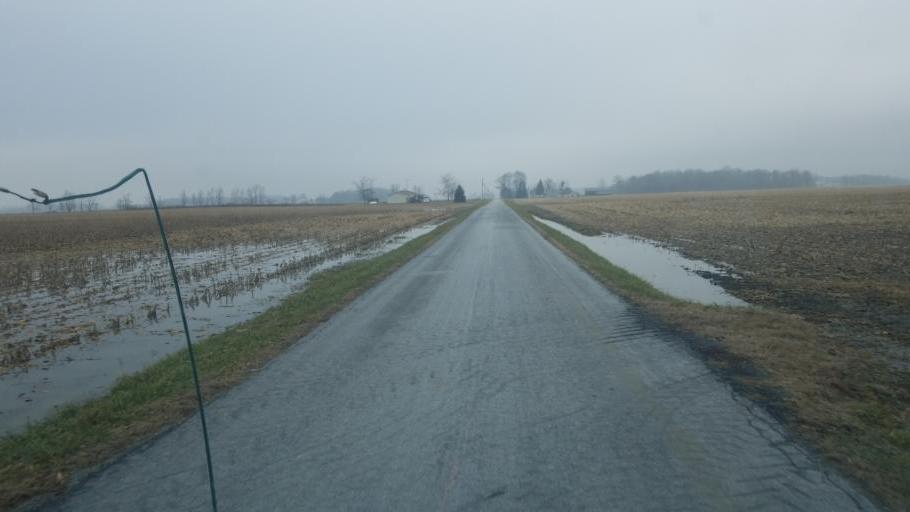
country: US
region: Ohio
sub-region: Hardin County
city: Forest
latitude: 40.6758
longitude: -83.4777
